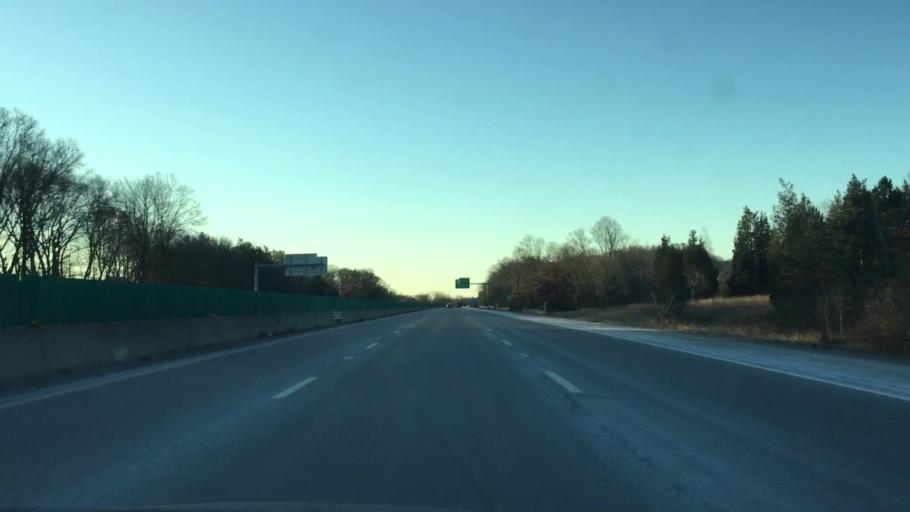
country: US
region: Massachusetts
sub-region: Norfolk County
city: Avon
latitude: 42.1083
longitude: -71.0588
